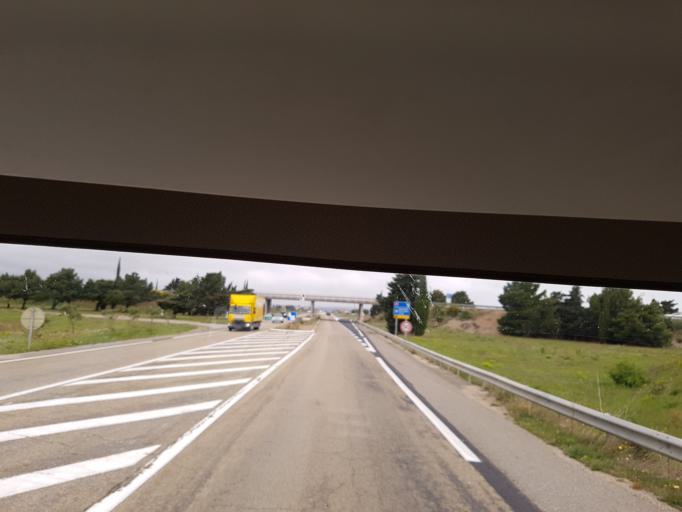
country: FR
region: Languedoc-Roussillon
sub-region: Departement de l'Aude
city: Leucate
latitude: 42.9351
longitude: 2.9917
